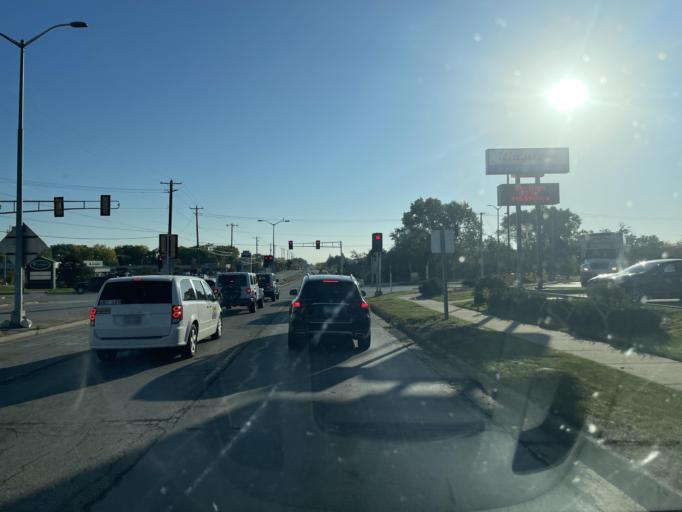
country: US
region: Wisconsin
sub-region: Kenosha County
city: Salem
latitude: 42.5682
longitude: -88.1171
